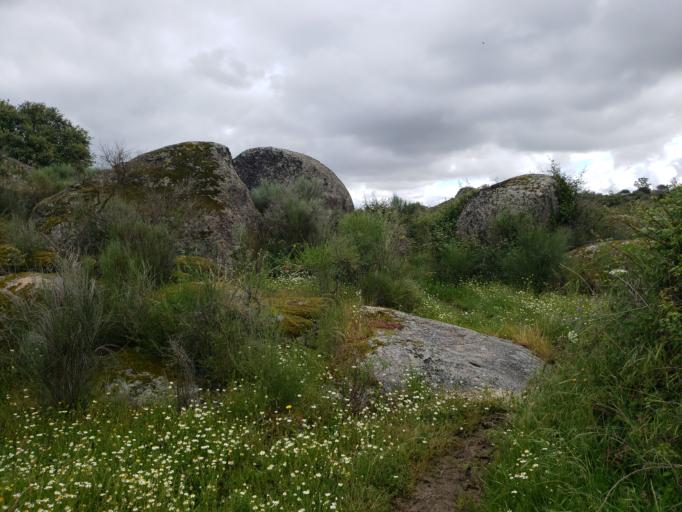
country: ES
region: Extremadura
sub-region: Provincia de Caceres
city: Malpartida de Caceres
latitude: 39.4250
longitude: -6.4949
